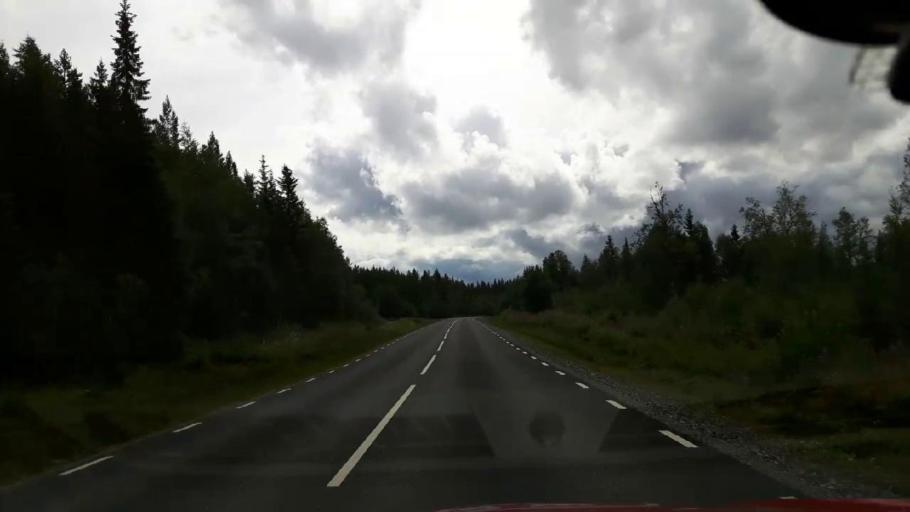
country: NO
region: Nord-Trondelag
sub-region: Lierne
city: Sandvika
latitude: 64.6009
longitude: 14.1206
